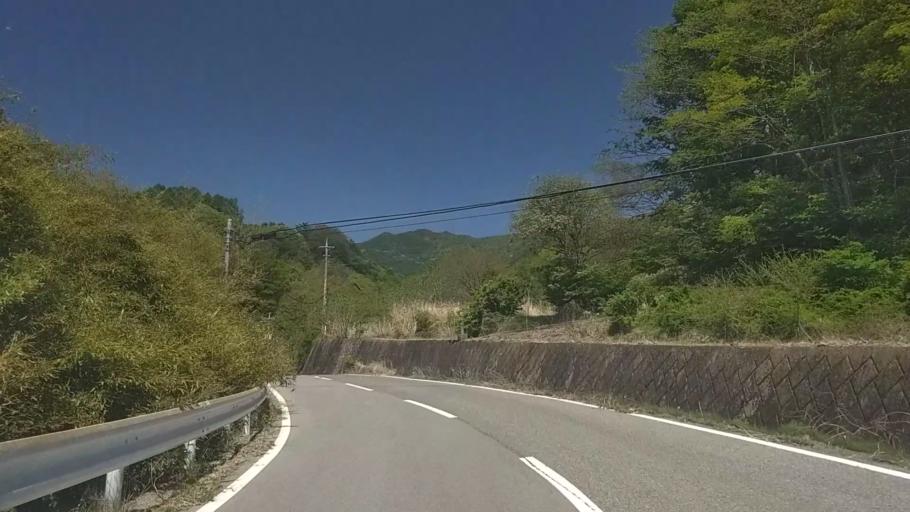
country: JP
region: Yamanashi
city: Nirasaki
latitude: 35.8822
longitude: 138.4586
